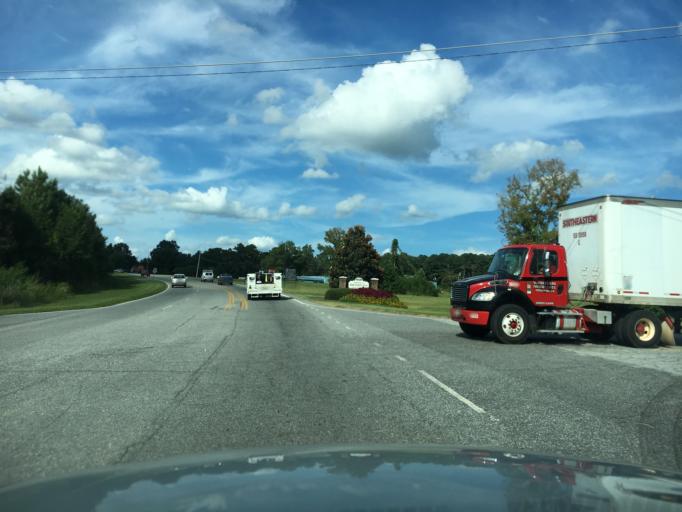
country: US
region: South Carolina
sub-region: Greenville County
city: Fountain Inn
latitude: 34.6817
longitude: -82.1998
